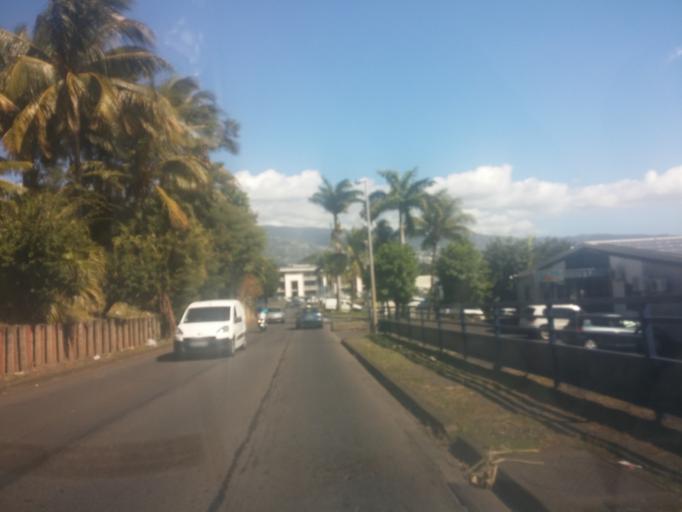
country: RE
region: Reunion
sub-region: Reunion
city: Sainte-Marie
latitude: -20.8991
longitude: 55.5291
